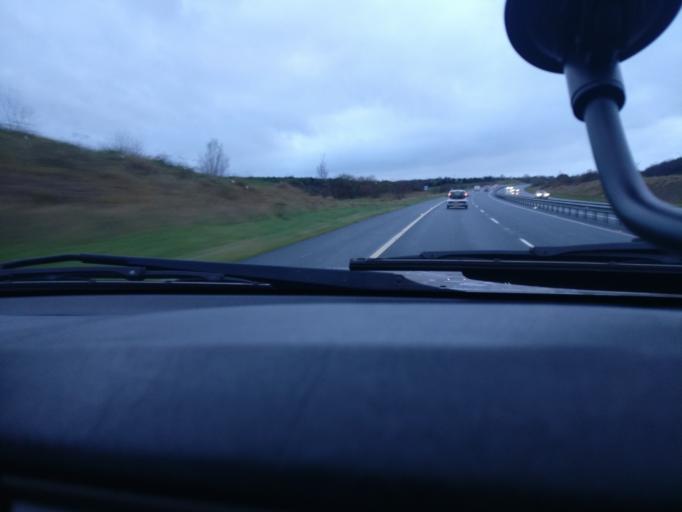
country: IE
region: Leinster
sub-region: An Iarmhi
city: Athlone
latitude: 53.3485
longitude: -8.0721
